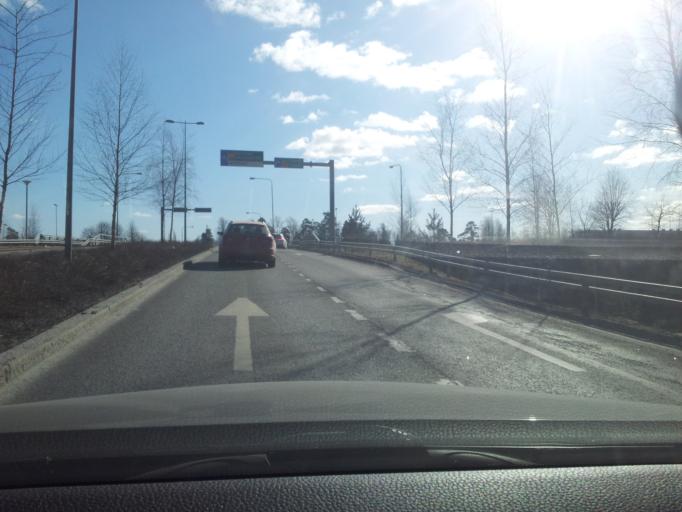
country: FI
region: Uusimaa
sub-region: Helsinki
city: Otaniemi
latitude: 60.1704
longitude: 24.8023
